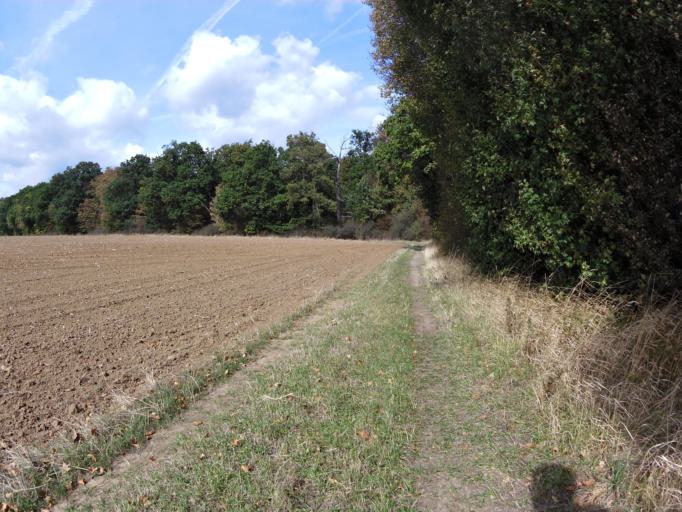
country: DE
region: Bavaria
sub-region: Regierungsbezirk Unterfranken
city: Reichenberg
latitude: 49.7351
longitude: 9.9434
